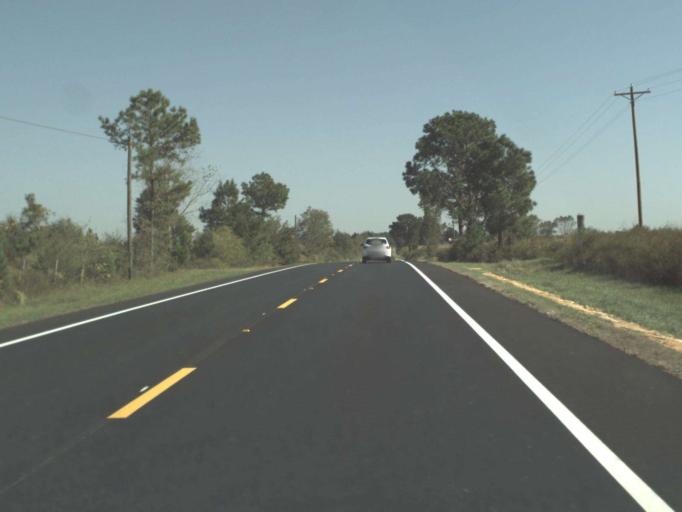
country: US
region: Alabama
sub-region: Covington County
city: Florala
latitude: 30.8808
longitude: -86.2700
